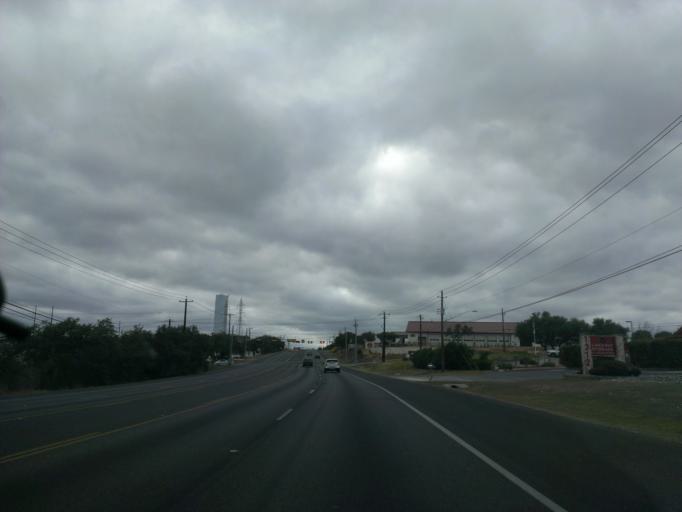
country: US
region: Texas
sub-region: Travis County
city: Lakeway
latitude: 30.3787
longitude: -97.9460
